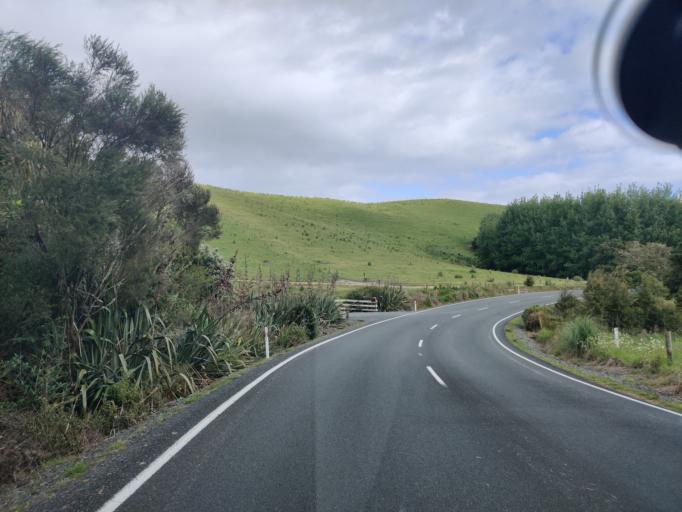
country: NZ
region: Northland
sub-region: Whangarei
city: Ngunguru
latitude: -35.5766
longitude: 174.3977
